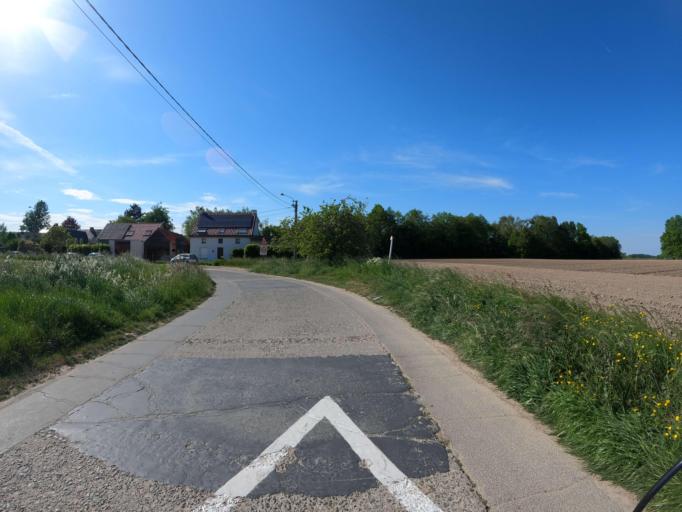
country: BE
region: Flanders
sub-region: Provincie Oost-Vlaanderen
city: Oosterzele
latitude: 50.9271
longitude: 3.7579
